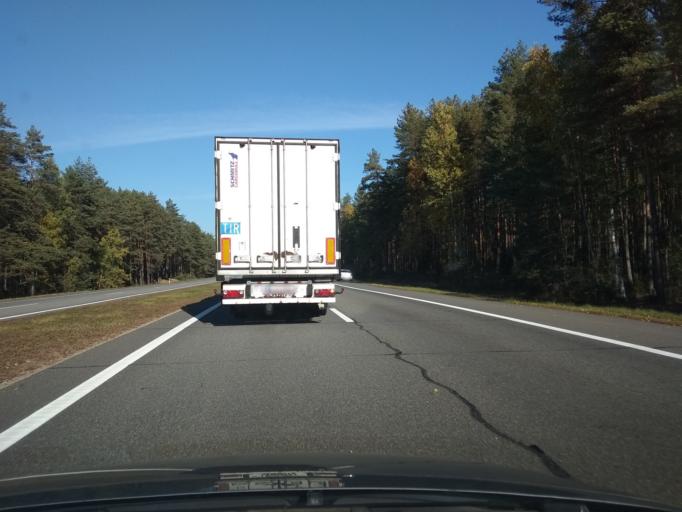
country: BY
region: Brest
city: Baranovichi
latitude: 52.9938
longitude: 25.7586
